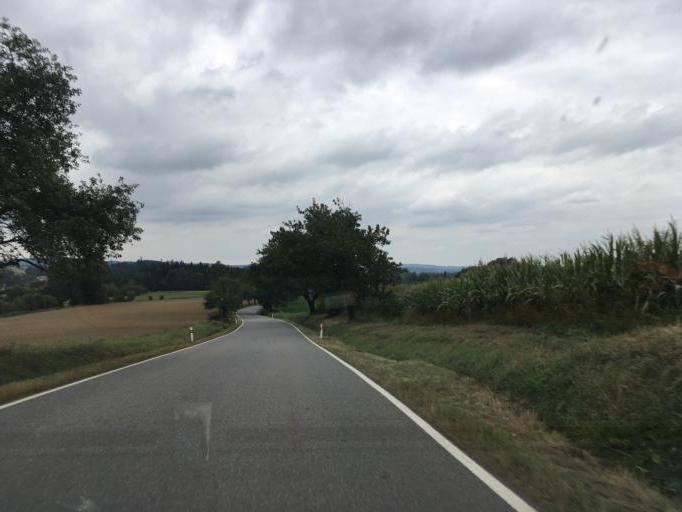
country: CZ
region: Vysocina
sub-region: Okres Jihlava
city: Telc
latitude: 49.2171
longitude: 15.4252
